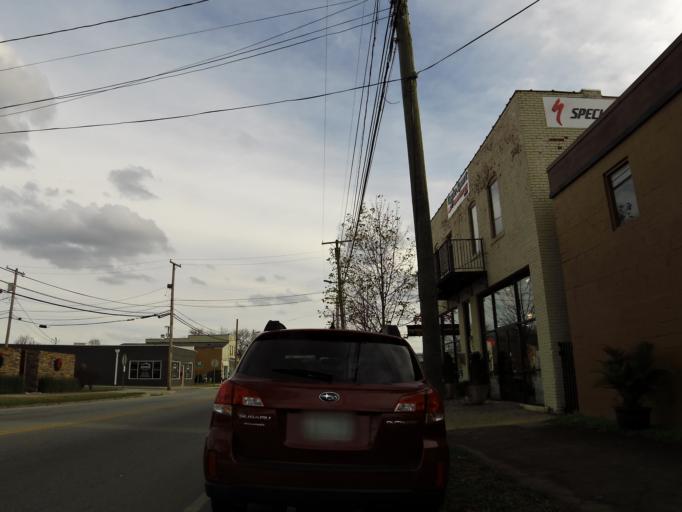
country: US
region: Tennessee
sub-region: Hamilton County
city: Chattanooga
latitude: 35.0336
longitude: -85.3008
